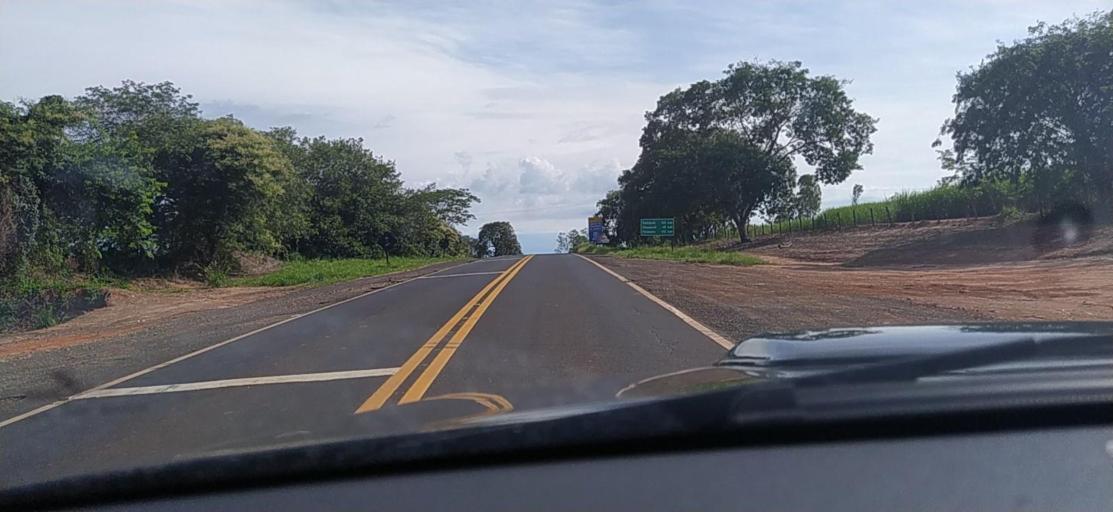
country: BR
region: Sao Paulo
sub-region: Catanduva
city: Catanduva
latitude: -21.0882
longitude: -49.0755
